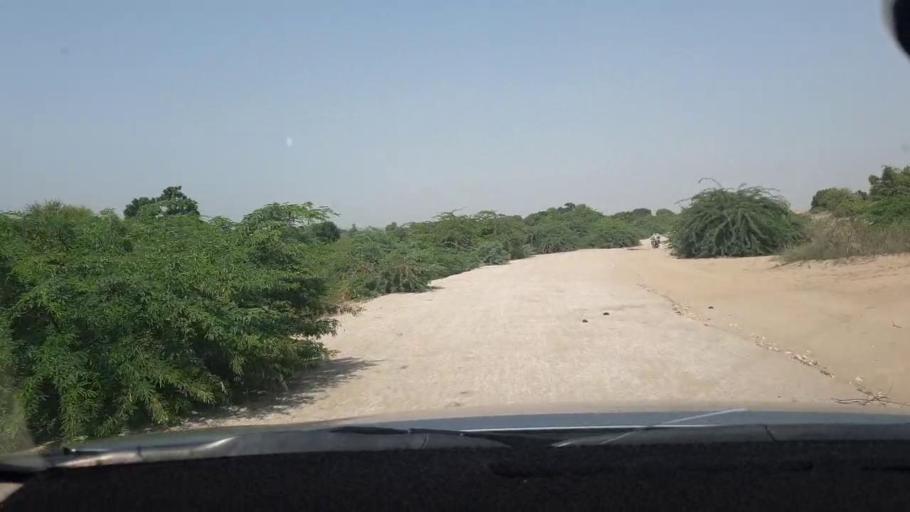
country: PK
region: Sindh
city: Tando Mittha Khan
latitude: 25.8467
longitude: 69.4243
